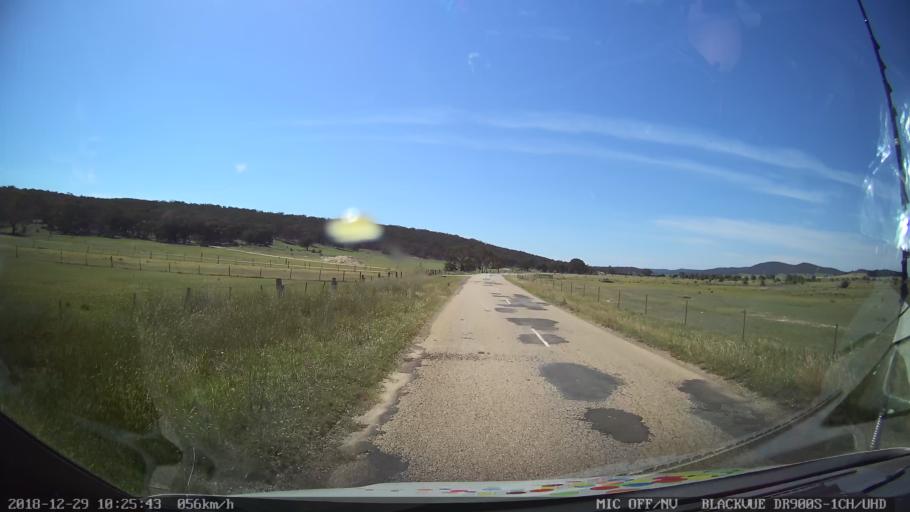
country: AU
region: New South Wales
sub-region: Yass Valley
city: Gundaroo
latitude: -34.9197
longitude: 149.4393
